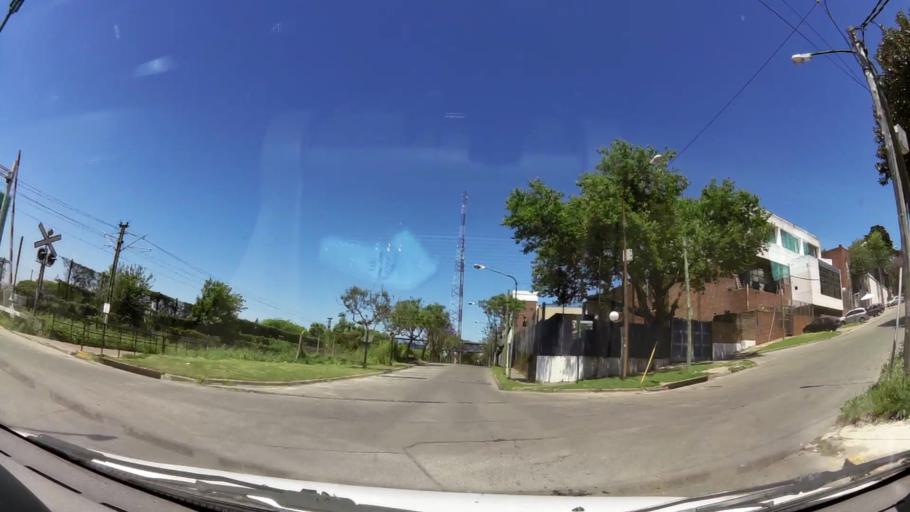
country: AR
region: Buenos Aires
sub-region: Partido de Vicente Lopez
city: Olivos
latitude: -34.4905
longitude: -58.4814
